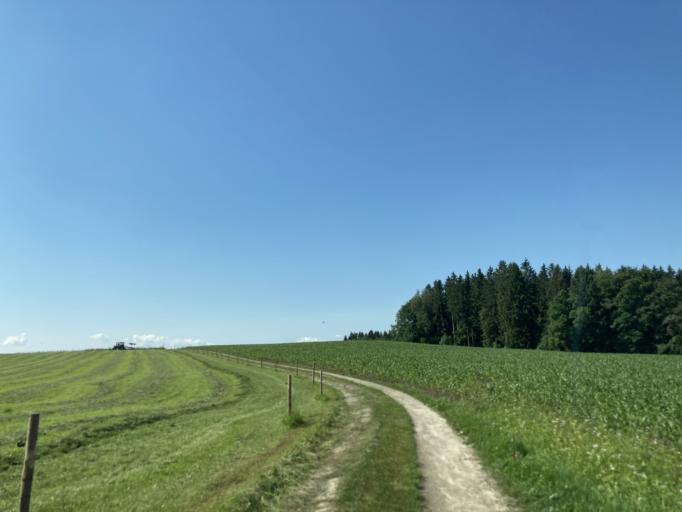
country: DE
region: Bavaria
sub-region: Upper Bavaria
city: Hoslwang
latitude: 47.9578
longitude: 12.3073
